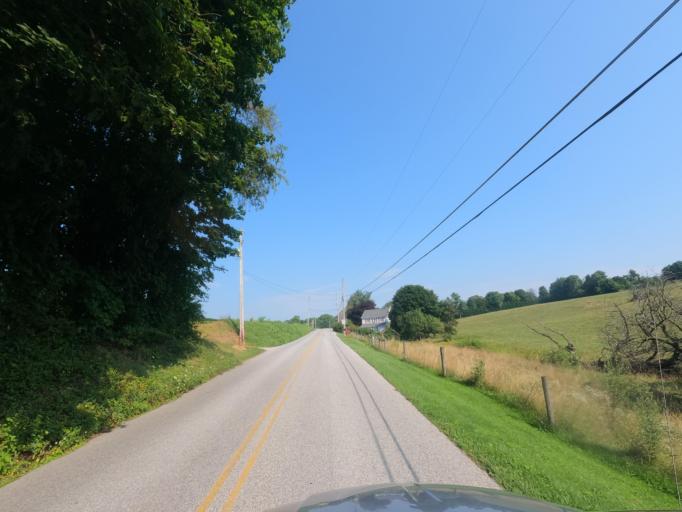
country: US
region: Pennsylvania
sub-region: York County
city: Shrewsbury
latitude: 39.7813
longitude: -76.6609
